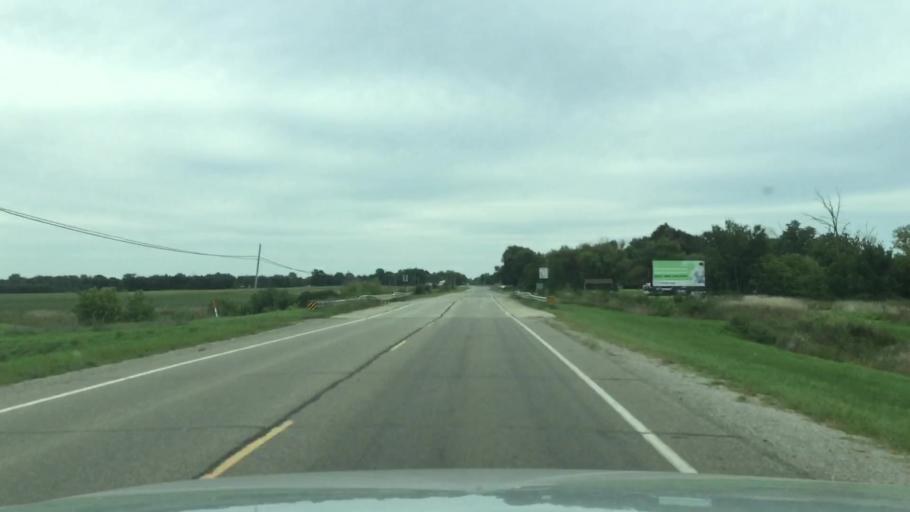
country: US
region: Michigan
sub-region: Shiawassee County
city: Durand
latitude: 42.9254
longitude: -83.9767
